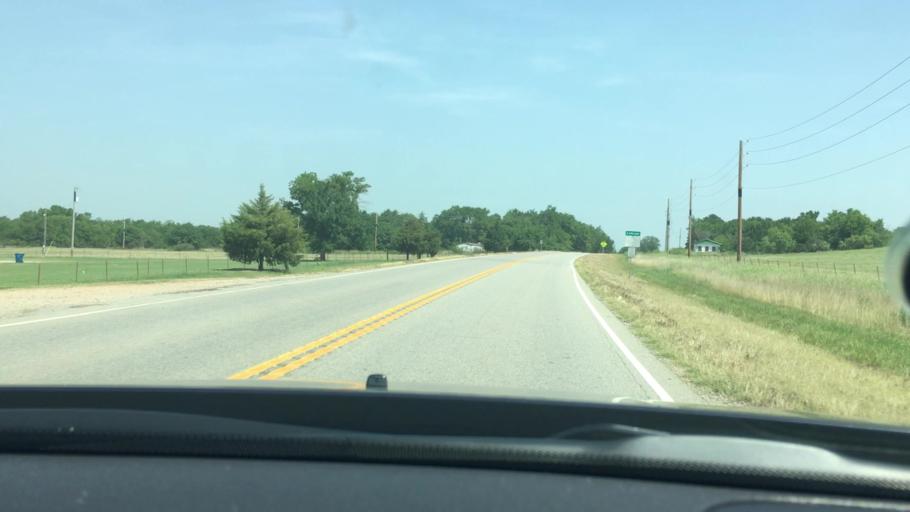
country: US
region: Oklahoma
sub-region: Coal County
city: Coalgate
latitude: 34.4631
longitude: -96.2166
